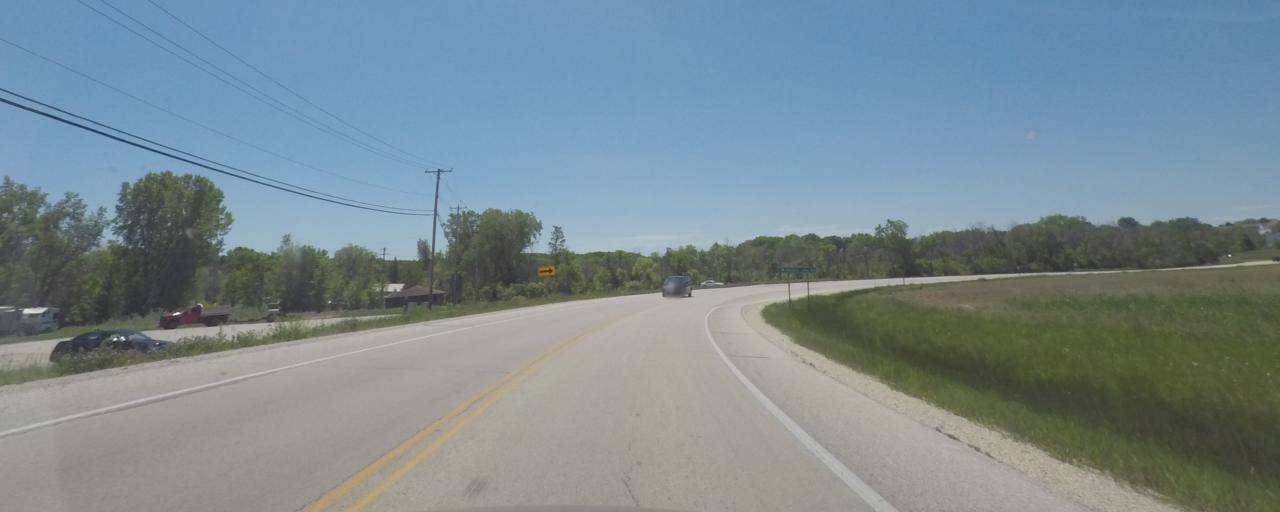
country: US
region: Wisconsin
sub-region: Washington County
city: West Bend
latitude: 43.4500
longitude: -88.1663
